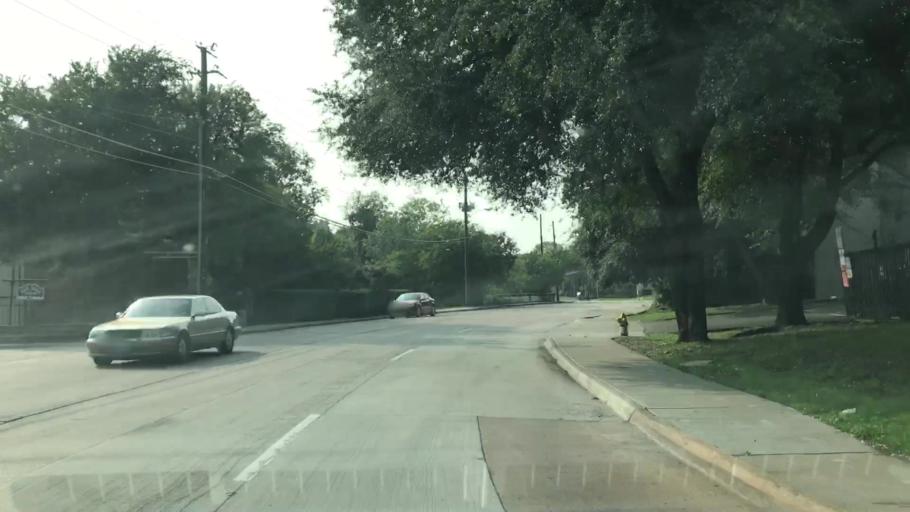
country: US
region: Texas
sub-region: Dallas County
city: Richardson
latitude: 32.9001
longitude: -96.7250
